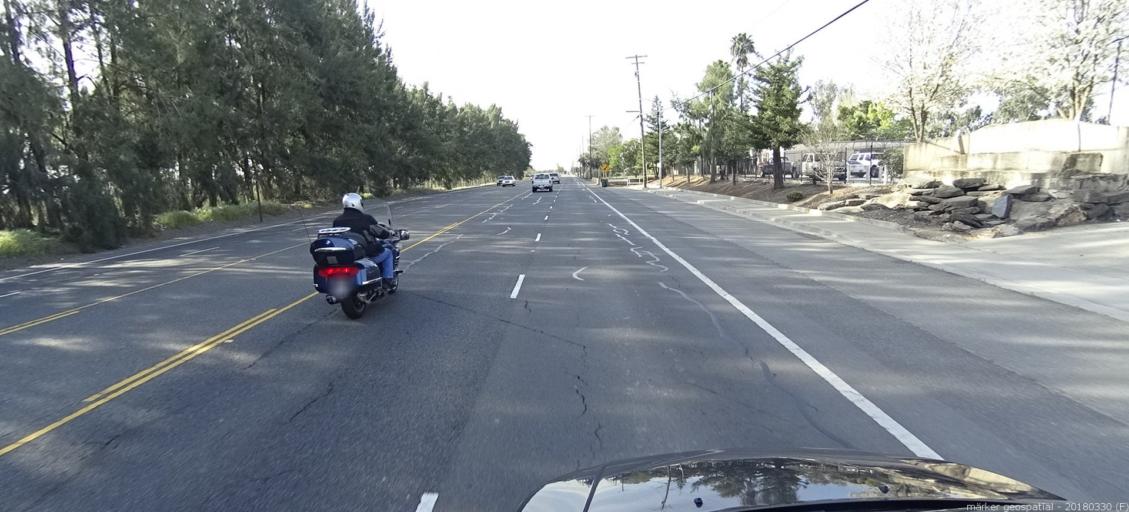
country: US
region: California
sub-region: Sacramento County
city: Vineyard
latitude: 38.5044
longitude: -121.3350
